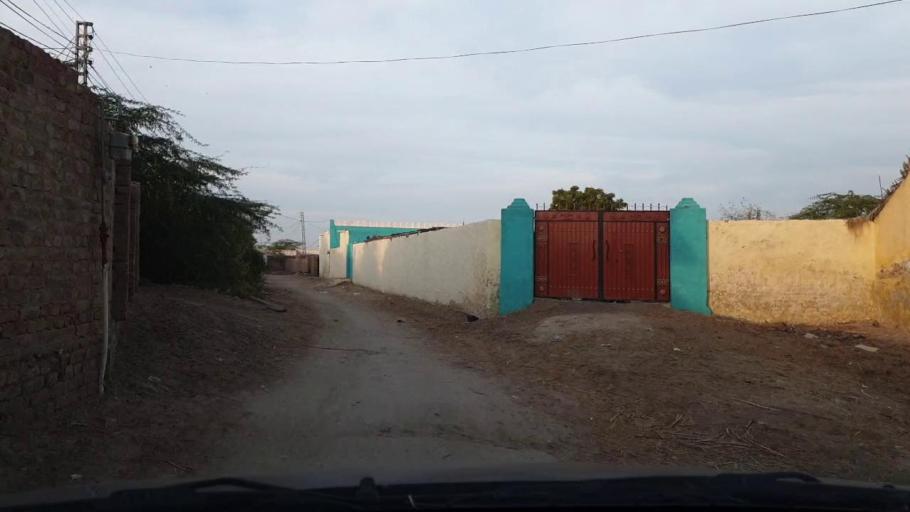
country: PK
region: Sindh
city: Khadro
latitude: 26.1394
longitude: 68.7462
